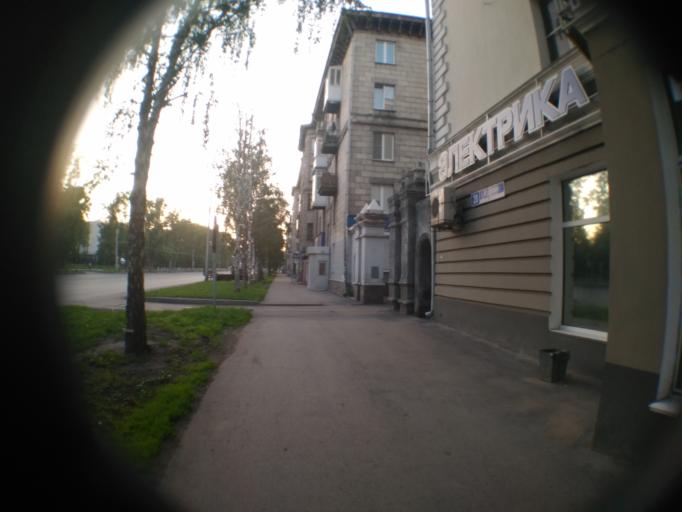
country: RU
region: Kemerovo
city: Novokuznetsk
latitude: 53.7552
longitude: 87.1083
